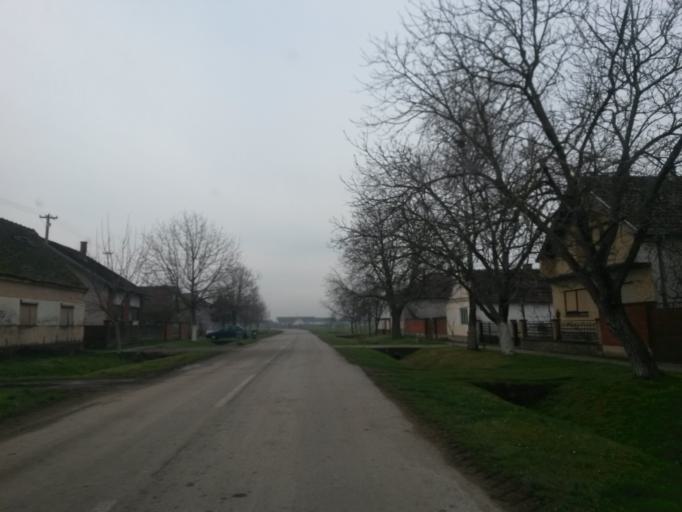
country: HR
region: Vukovarsko-Srijemska
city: Markusica
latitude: 45.3714
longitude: 18.6963
